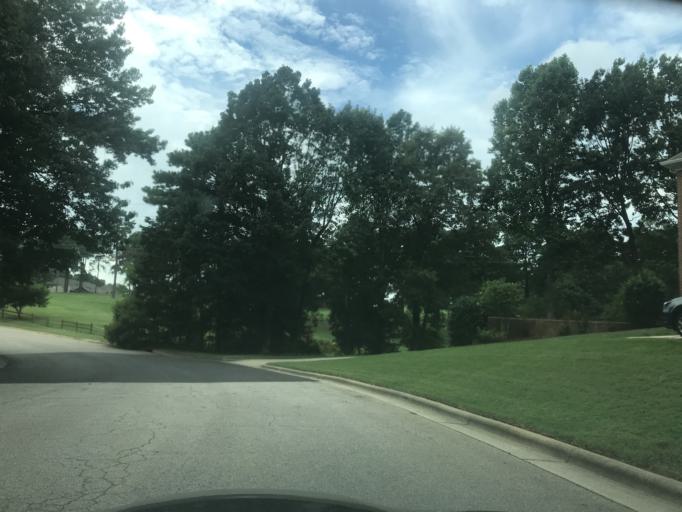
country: US
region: North Carolina
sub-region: Wake County
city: West Raleigh
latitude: 35.8890
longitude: -78.6069
